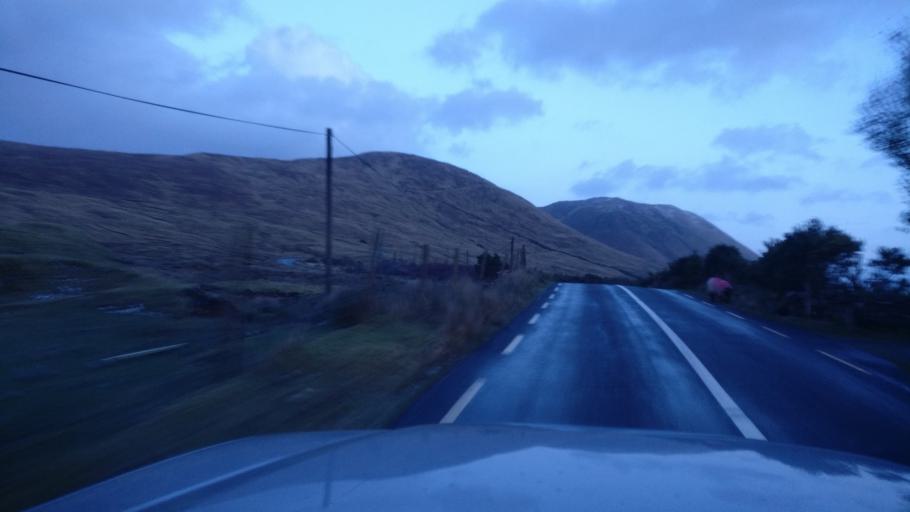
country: IE
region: Connaught
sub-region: Maigh Eo
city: Westport
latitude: 53.5821
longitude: -9.6756
